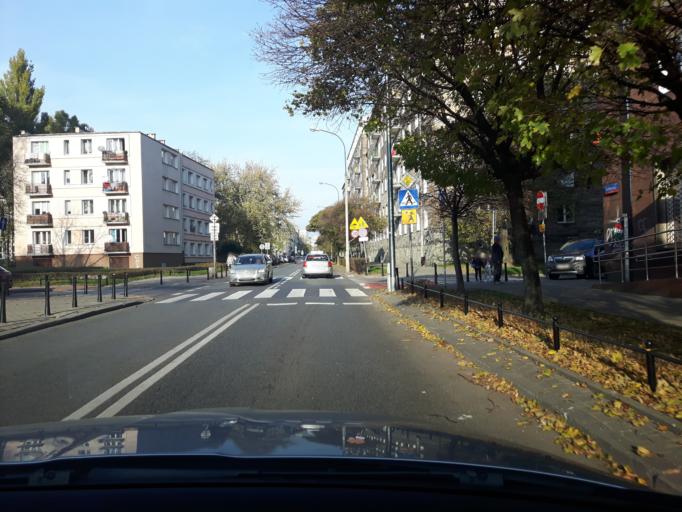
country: PL
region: Masovian Voivodeship
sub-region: Warszawa
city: Ochota
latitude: 52.2140
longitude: 20.9741
